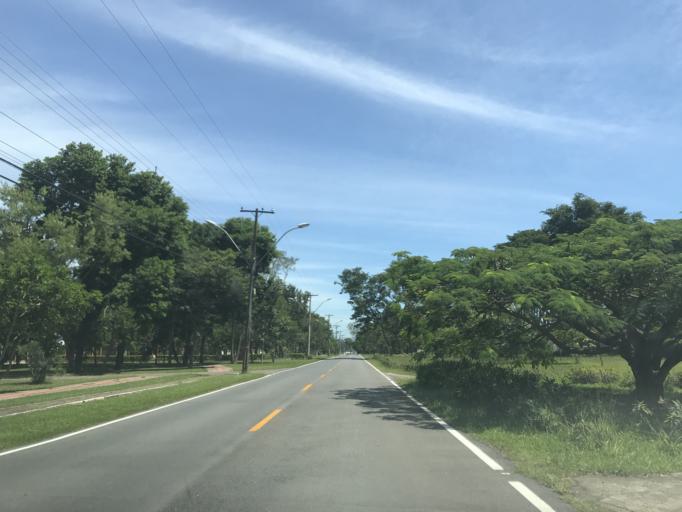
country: BR
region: Federal District
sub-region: Brasilia
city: Brasilia
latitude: -15.9039
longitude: -47.9335
